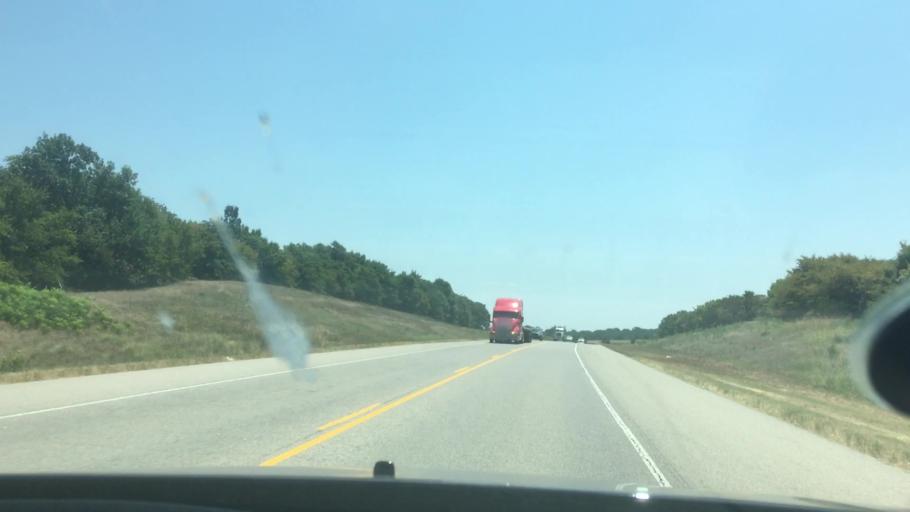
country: US
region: Oklahoma
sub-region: Pontotoc County
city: Ada
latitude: 34.6770
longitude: -96.5766
